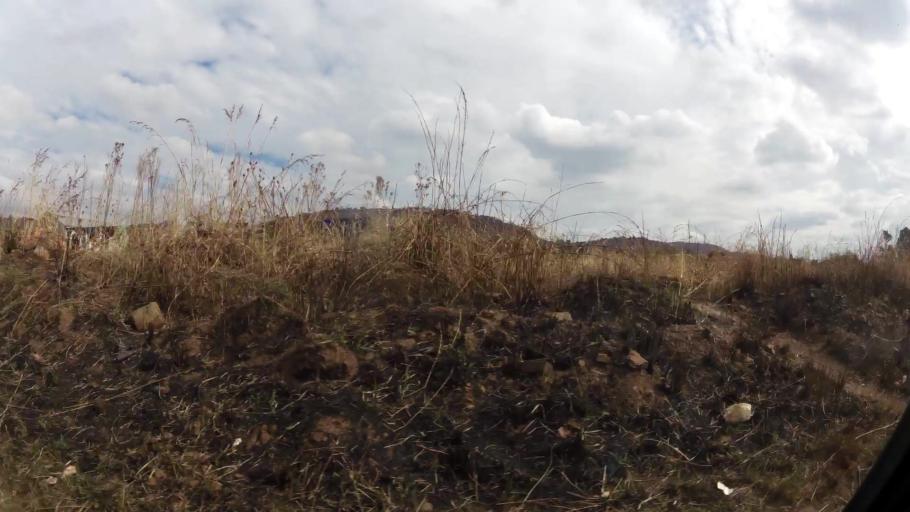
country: ZA
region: Gauteng
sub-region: City of Johannesburg Metropolitan Municipality
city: Roodepoort
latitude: -26.1036
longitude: 27.8811
